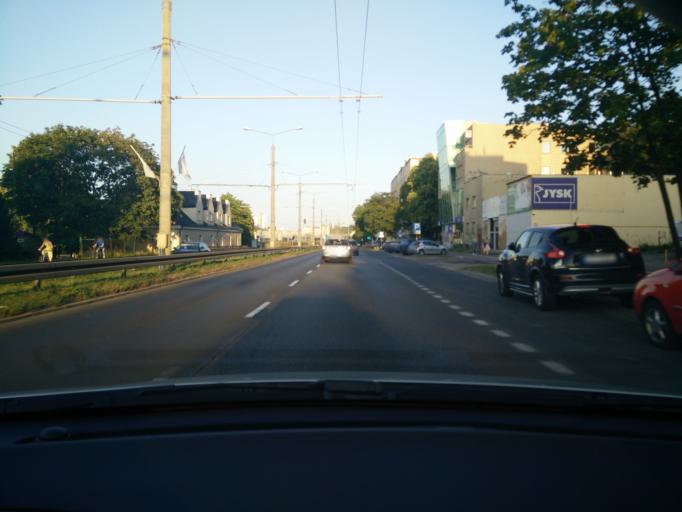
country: PL
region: Pomeranian Voivodeship
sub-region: Gdynia
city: Gdynia
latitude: 54.5237
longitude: 18.5200
